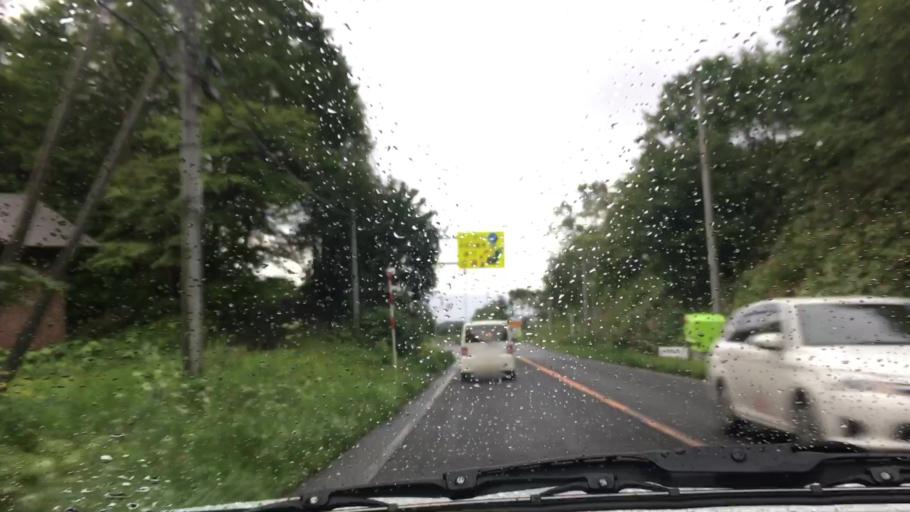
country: JP
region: Hokkaido
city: Date
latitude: 42.5927
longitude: 140.7213
